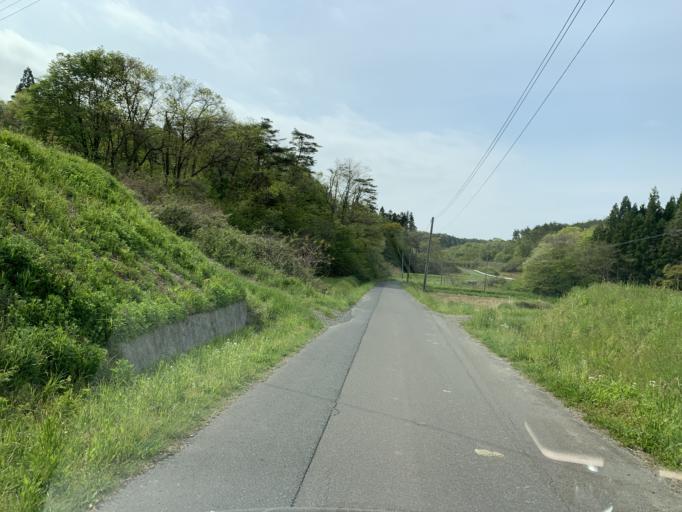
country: JP
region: Iwate
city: Ichinoseki
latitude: 38.9034
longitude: 141.0570
